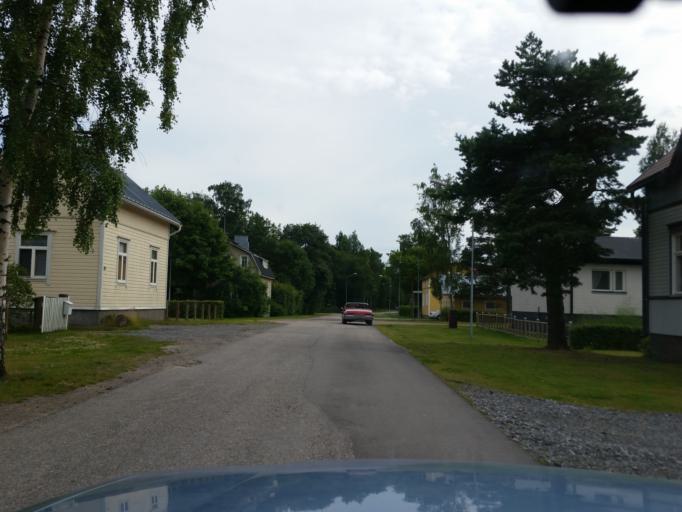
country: FI
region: Uusimaa
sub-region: Raaseporin
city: Hanko
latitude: 59.8377
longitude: 22.9542
